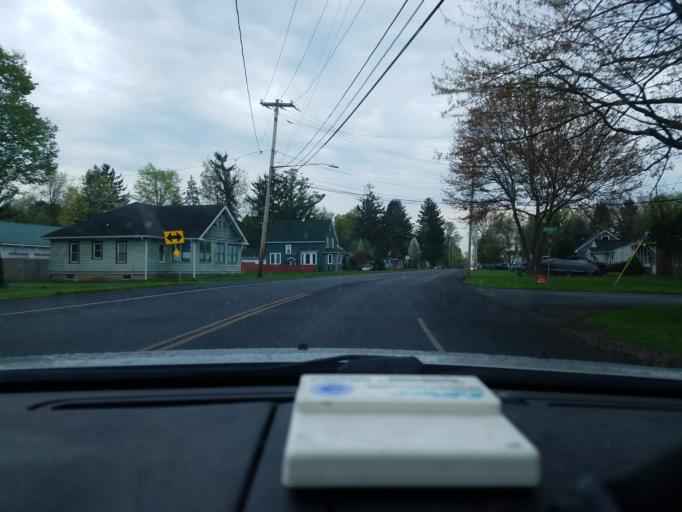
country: US
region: New York
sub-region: Onondaga County
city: North Syracuse
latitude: 43.1333
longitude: -76.1149
